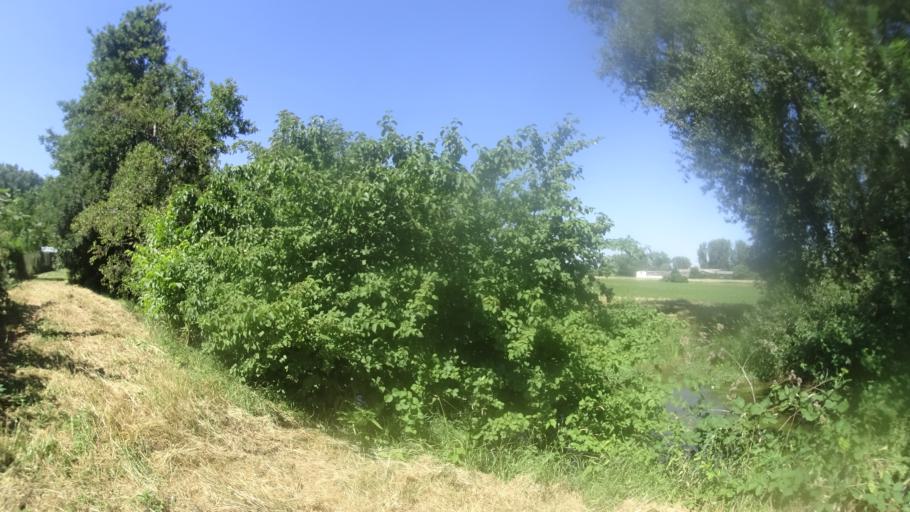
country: DE
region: Baden-Wuerttemberg
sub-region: Karlsruhe Region
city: Karlsruhe
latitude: 49.0065
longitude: 8.4618
